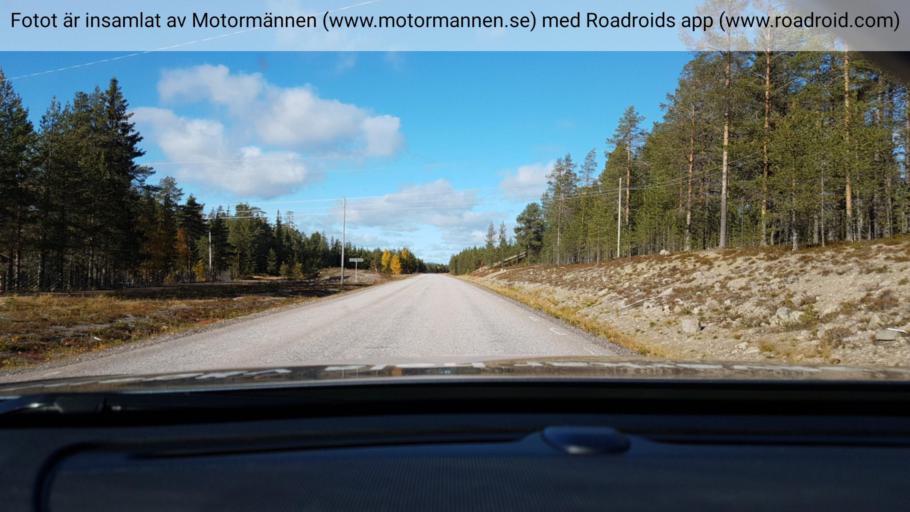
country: SE
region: Norrbotten
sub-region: Arvidsjaurs Kommun
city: Arvidsjaur
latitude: 65.7288
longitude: 18.6603
